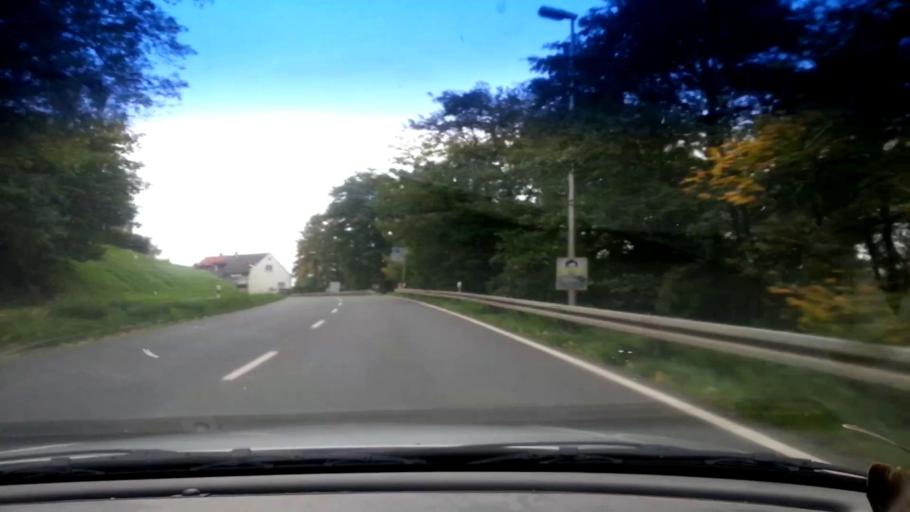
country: DE
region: Bavaria
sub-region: Upper Franconia
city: Baunach
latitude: 49.9837
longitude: 10.8550
